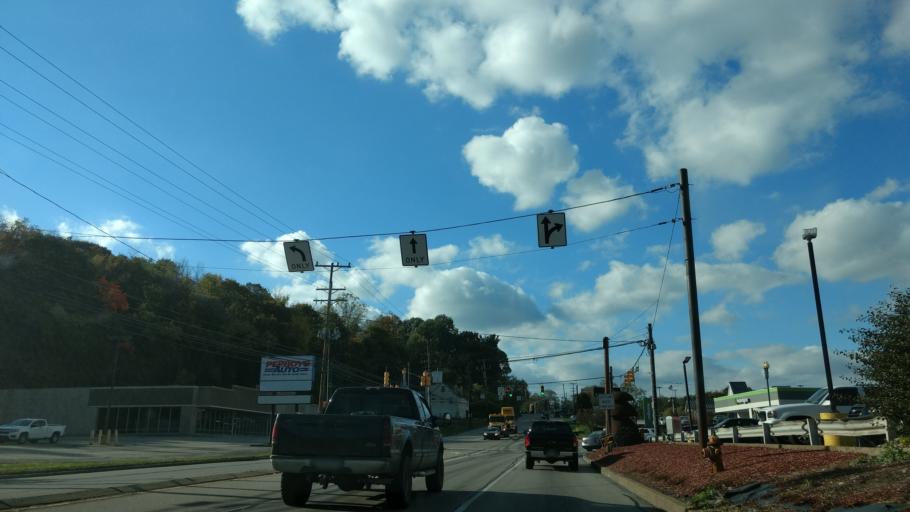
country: US
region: Pennsylvania
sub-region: Allegheny County
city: Pleasant Hills
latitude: 40.3374
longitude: -79.9507
